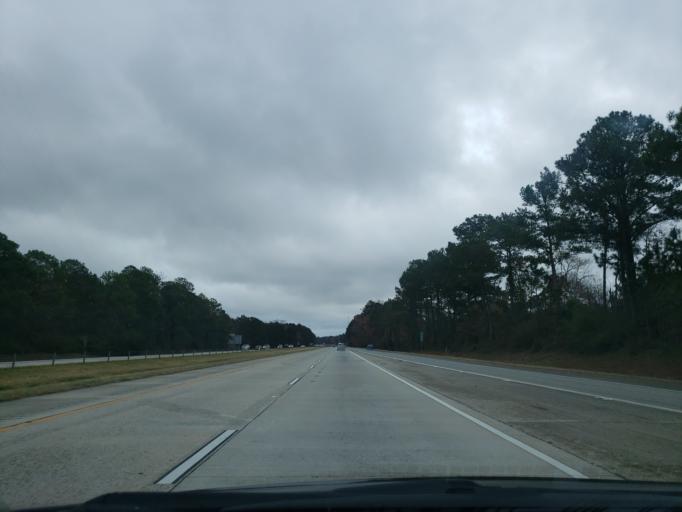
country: US
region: Georgia
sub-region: Laurens County
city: Dublin
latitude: 32.4872
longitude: -82.9324
